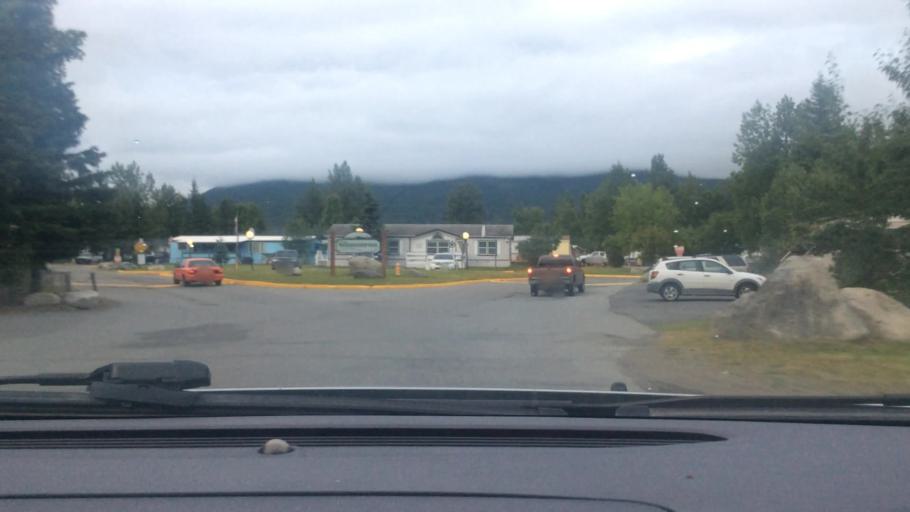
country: US
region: Alaska
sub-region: Anchorage Municipality
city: Elmendorf Air Force Base
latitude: 61.2003
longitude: -149.7303
